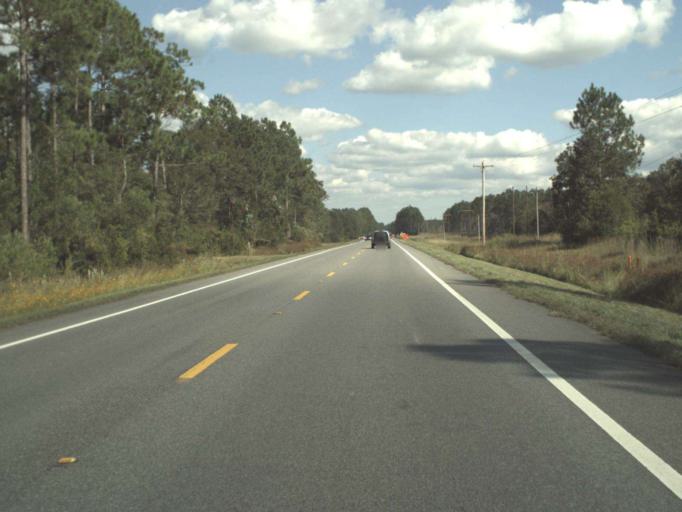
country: US
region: Florida
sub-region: Walton County
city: Freeport
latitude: 30.4743
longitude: -85.9934
